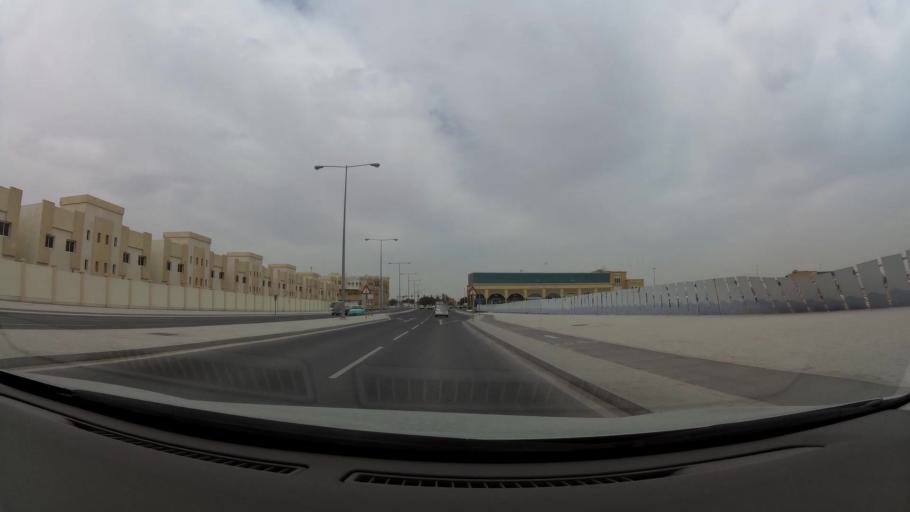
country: QA
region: Baladiyat ar Rayyan
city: Ar Rayyan
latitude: 25.2313
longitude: 51.4470
